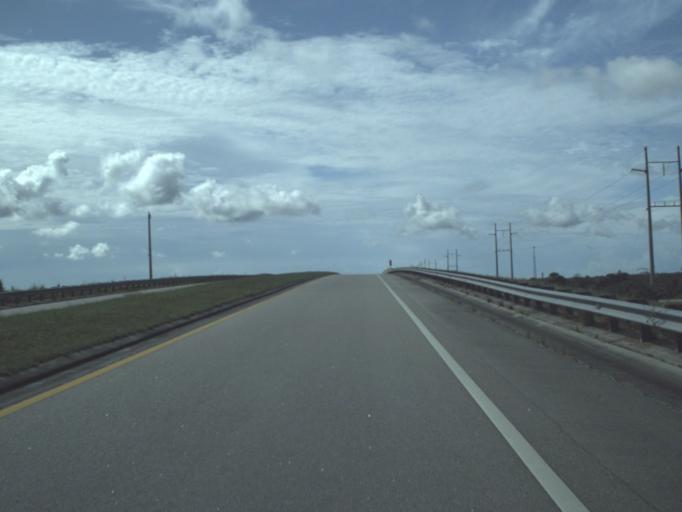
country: US
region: Florida
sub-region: Collier County
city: Immokalee
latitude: 26.1565
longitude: -81.3452
